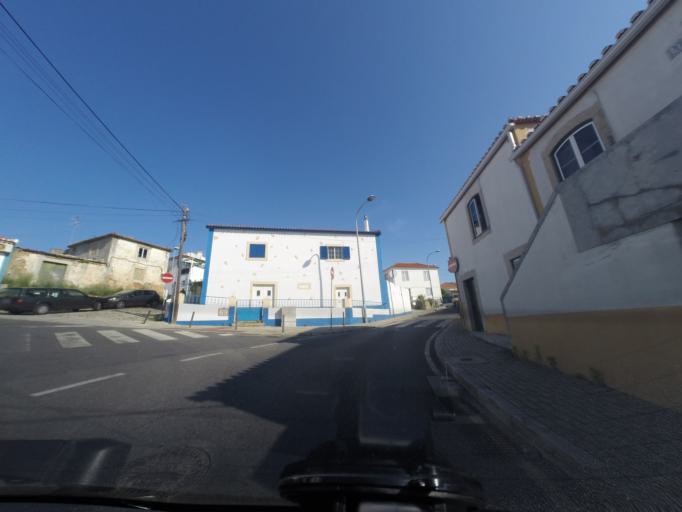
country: PT
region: Lisbon
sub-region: Cascais
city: Alcabideche
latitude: 38.7360
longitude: -9.3676
